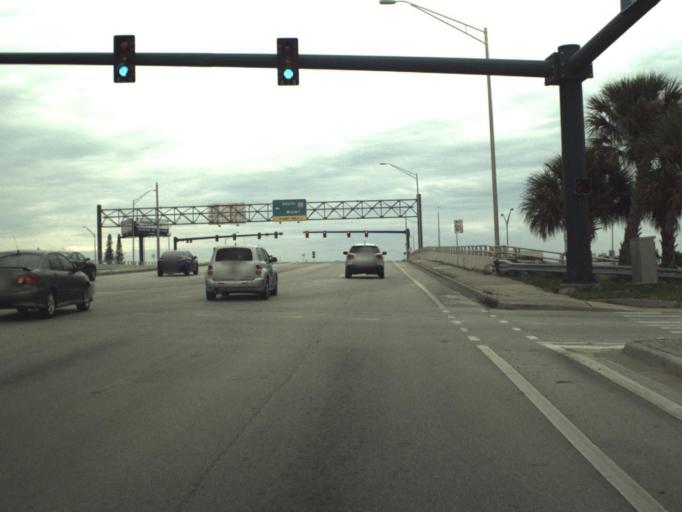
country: US
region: Florida
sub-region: Palm Beach County
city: Lake Clarke Shores
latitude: 26.6763
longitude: -80.0682
